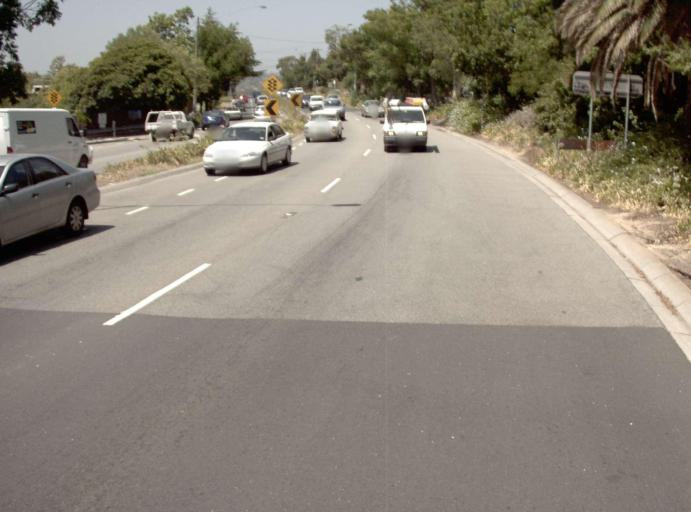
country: AU
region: Victoria
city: Rosanna
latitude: -37.7585
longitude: 145.0597
